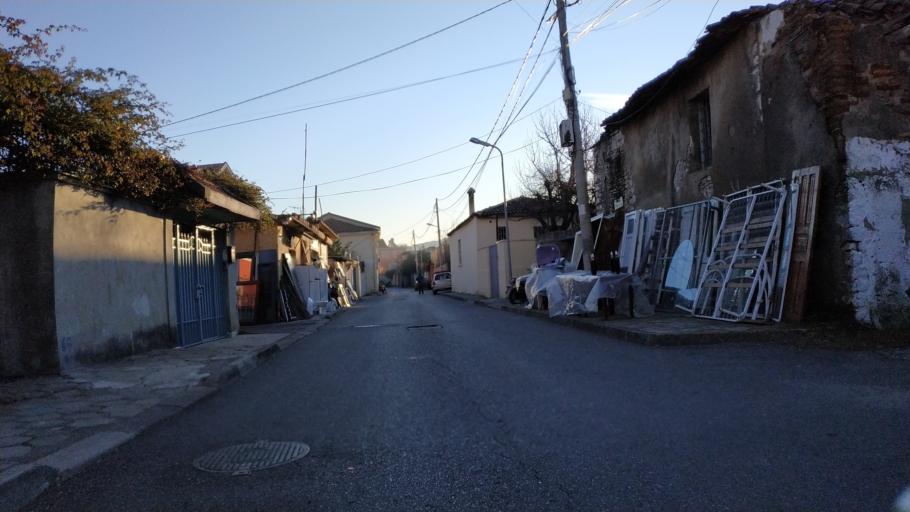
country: AL
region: Shkoder
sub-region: Rrethi i Shkodres
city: Shkoder
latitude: 42.0610
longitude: 19.5154
